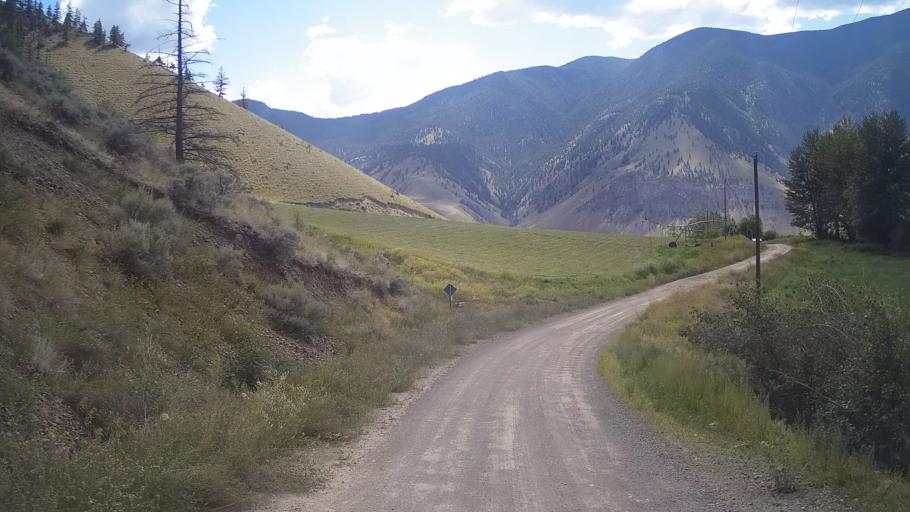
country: CA
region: British Columbia
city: Lillooet
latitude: 51.1964
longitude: -122.1123
